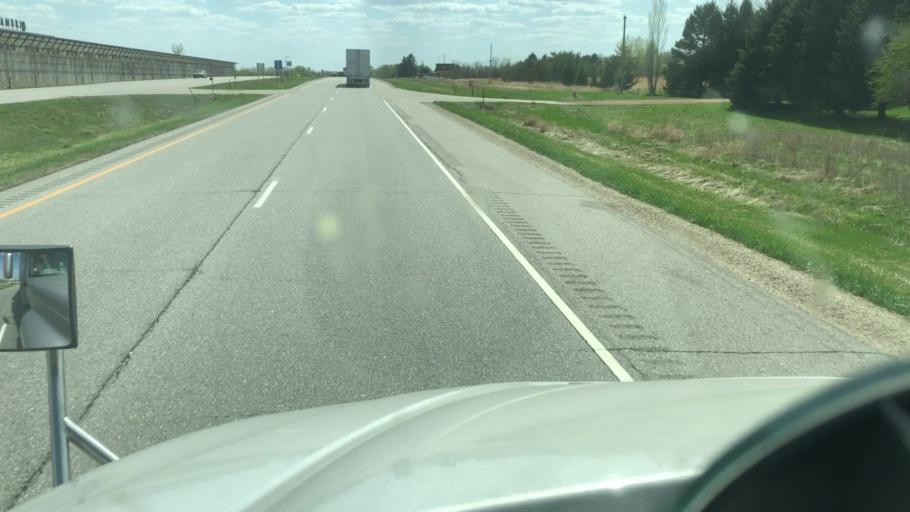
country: US
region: Minnesota
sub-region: Le Sueur County
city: Le Sueur
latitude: 44.4949
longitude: -93.8726
